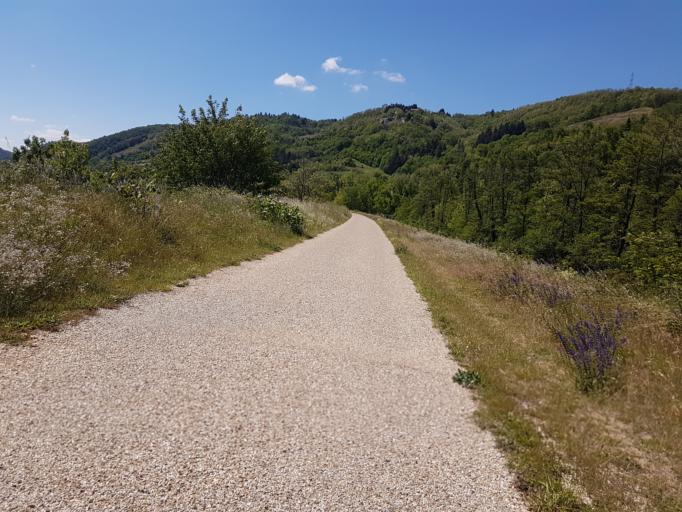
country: FR
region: Rhone-Alpes
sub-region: Departement de la Drome
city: Saint-Vallier
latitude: 45.1731
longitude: 4.8074
